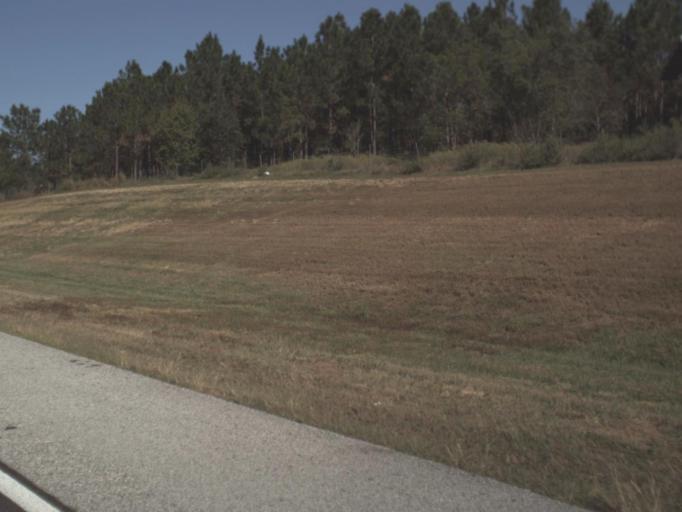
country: US
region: Florida
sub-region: Lake County
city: Montverde
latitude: 28.5773
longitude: -81.7011
